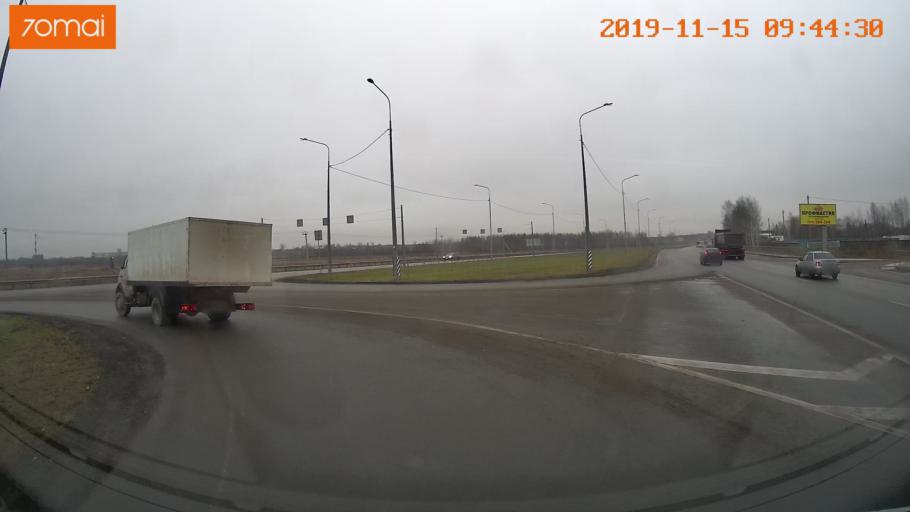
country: RU
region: Vologda
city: Sheksna
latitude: 59.2115
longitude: 38.5279
